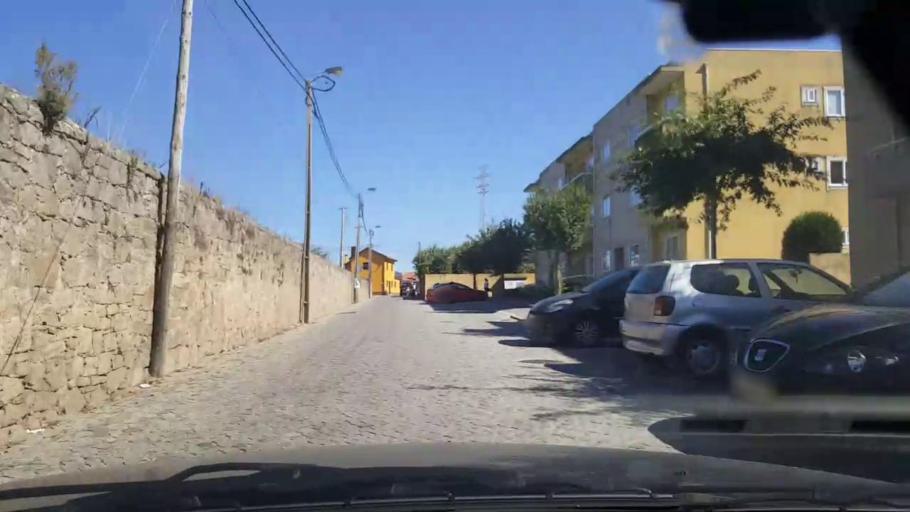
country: PT
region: Porto
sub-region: Vila do Conde
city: Arvore
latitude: 41.3110
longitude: -8.6787
